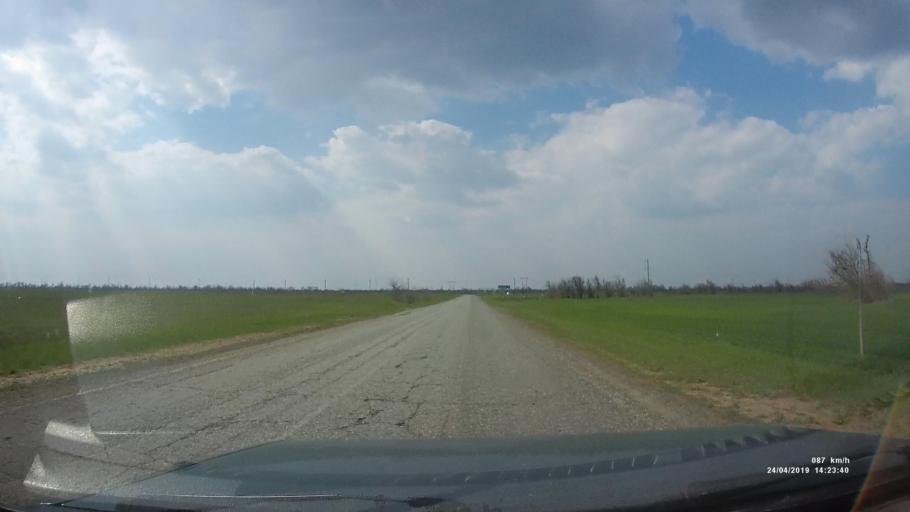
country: RU
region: Kalmykiya
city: Arshan'
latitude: 46.3240
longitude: 44.1111
